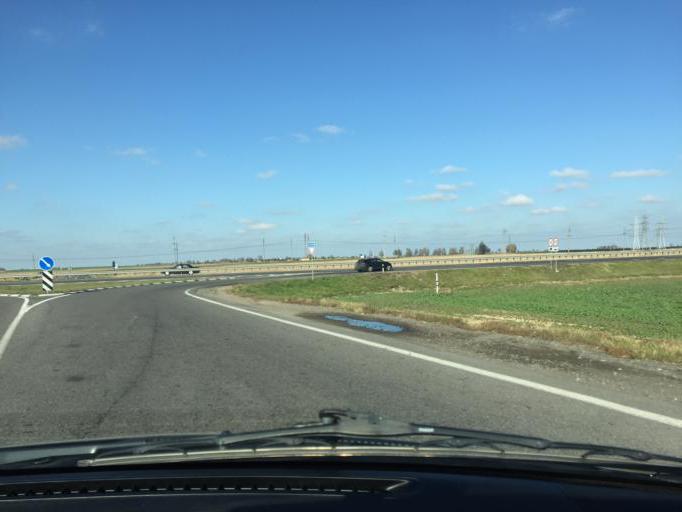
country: BY
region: Minsk
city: Slutsk
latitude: 53.0499
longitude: 27.5304
